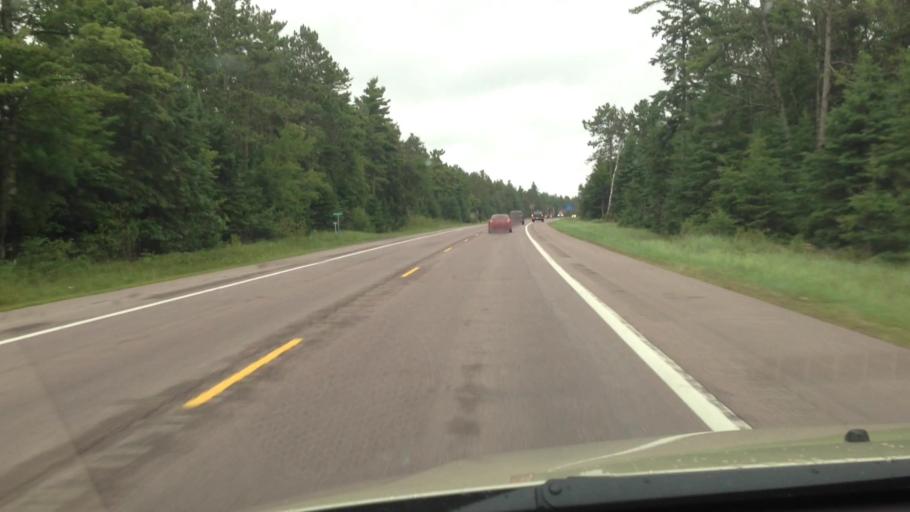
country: US
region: Michigan
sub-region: Schoolcraft County
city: Manistique
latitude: 45.9143
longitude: -86.3190
